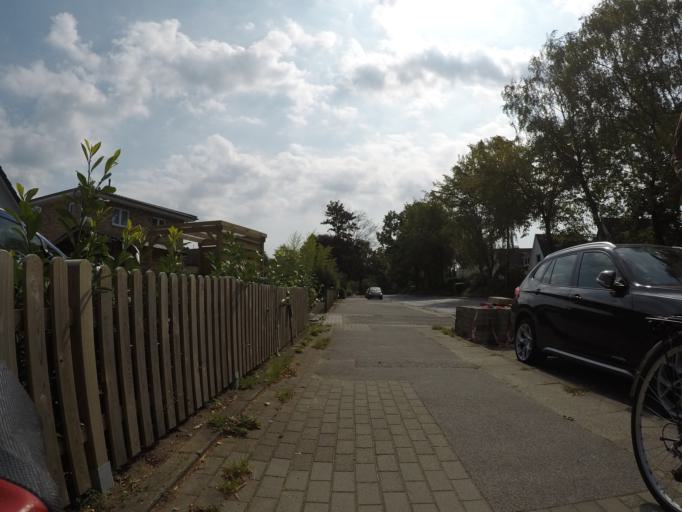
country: DE
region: Hamburg
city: Poppenbuettel
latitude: 53.6726
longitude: 10.0586
